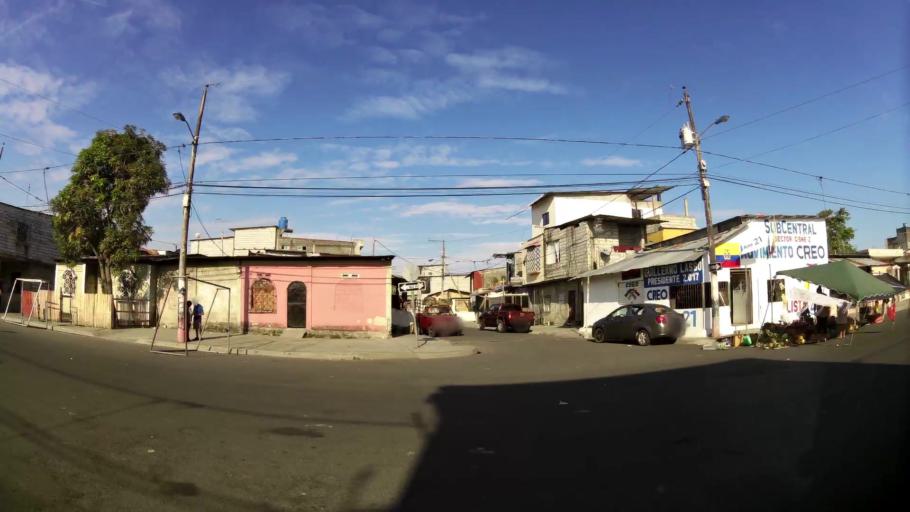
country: EC
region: Guayas
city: Guayaquil
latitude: -2.2233
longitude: -79.9198
